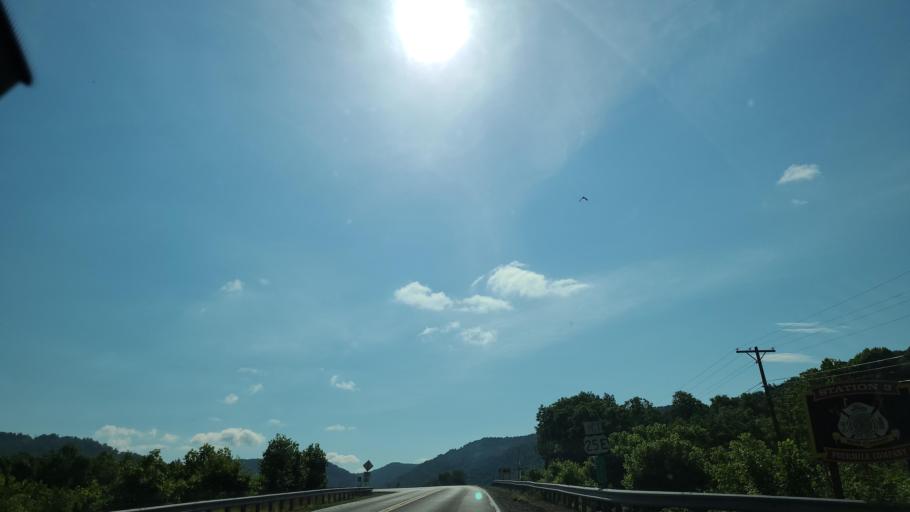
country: US
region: Kentucky
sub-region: Bell County
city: Pineville
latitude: 36.7901
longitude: -83.7497
